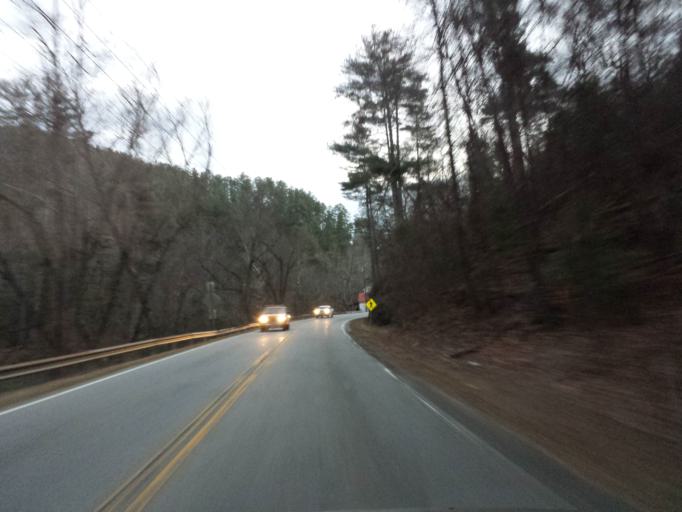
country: US
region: Georgia
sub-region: White County
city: Cleveland
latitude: 34.6911
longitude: -83.7127
